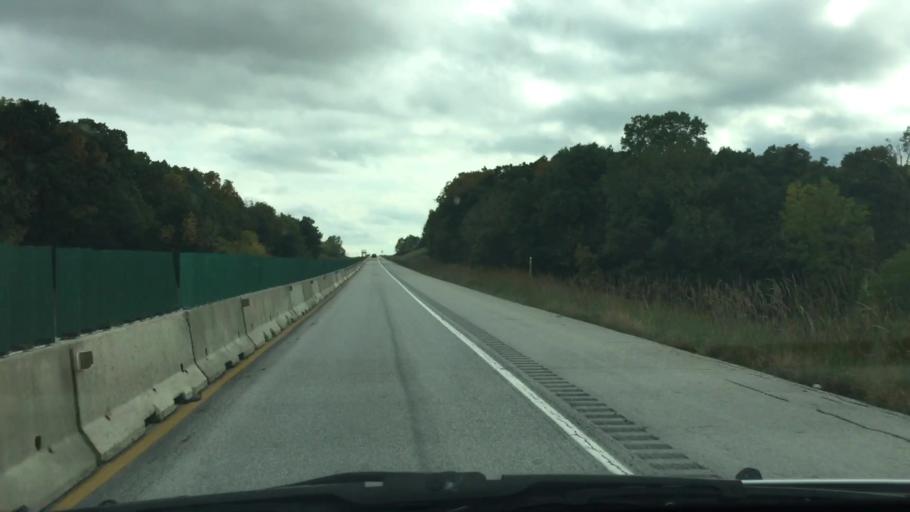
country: US
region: Iowa
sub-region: Decatur County
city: Leon
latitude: 40.6965
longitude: -93.8461
